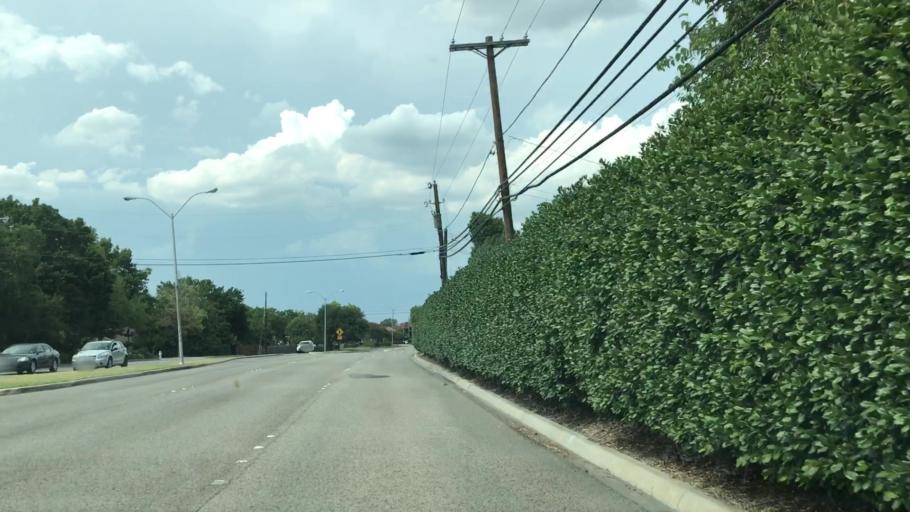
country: US
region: Texas
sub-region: Dallas County
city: Carrollton
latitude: 32.9422
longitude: -96.8730
